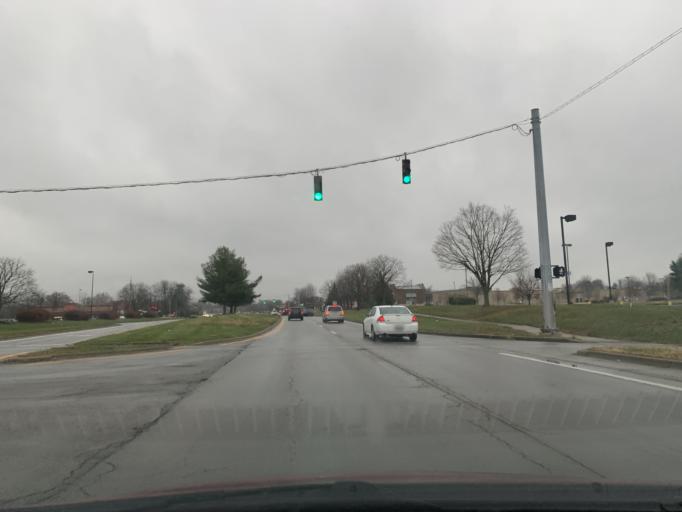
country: US
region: Kentucky
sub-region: Jefferson County
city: Hurstbourne Acres
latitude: 38.2119
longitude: -85.5956
